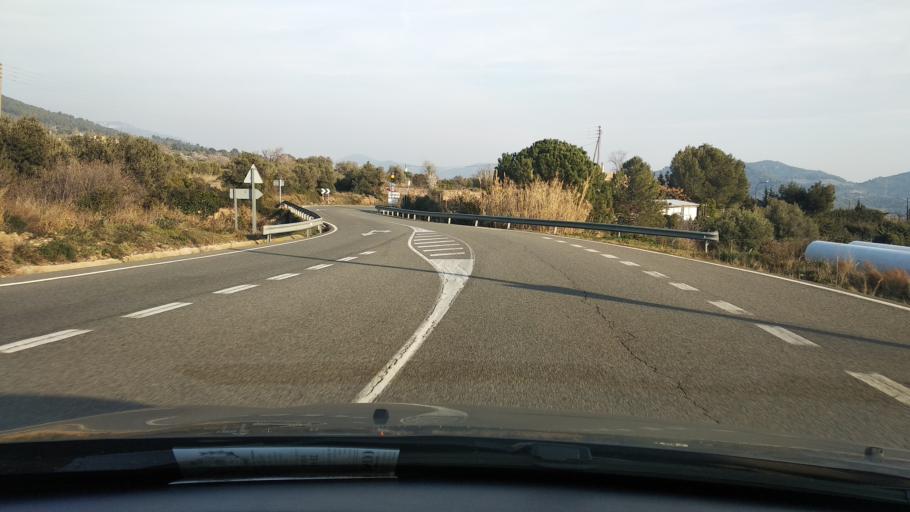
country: ES
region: Catalonia
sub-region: Provincia de Tarragona
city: Alforja
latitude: 41.2152
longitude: 0.9748
